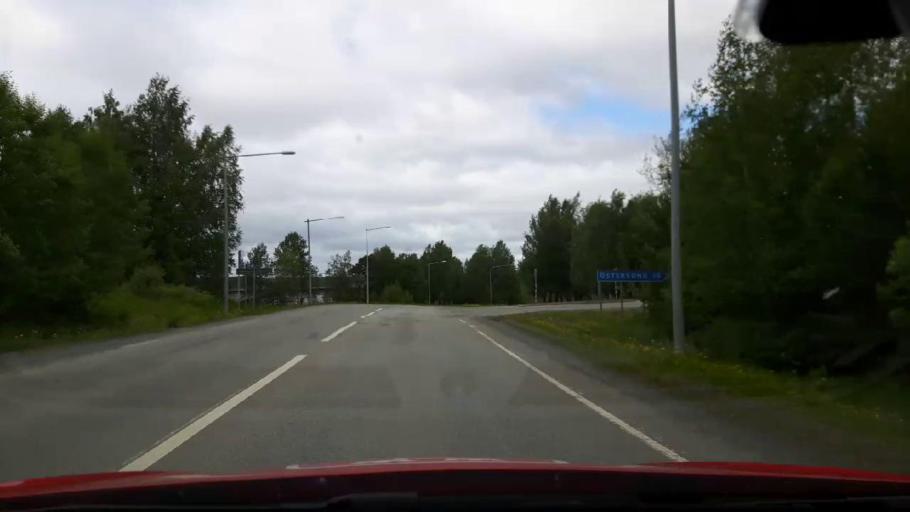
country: SE
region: Jaemtland
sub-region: Krokoms Kommun
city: Krokom
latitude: 63.3140
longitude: 14.4567
